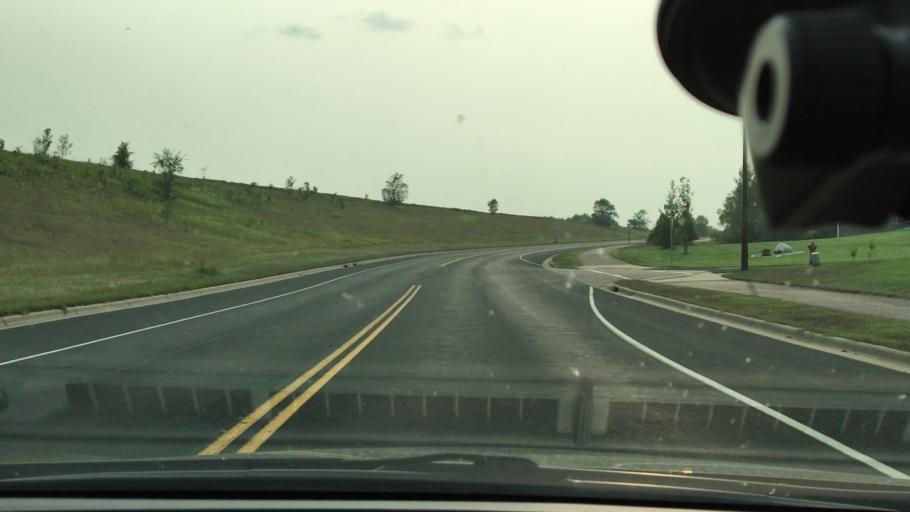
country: US
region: Minnesota
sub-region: Wright County
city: Otsego
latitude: 45.2601
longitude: -93.5843
